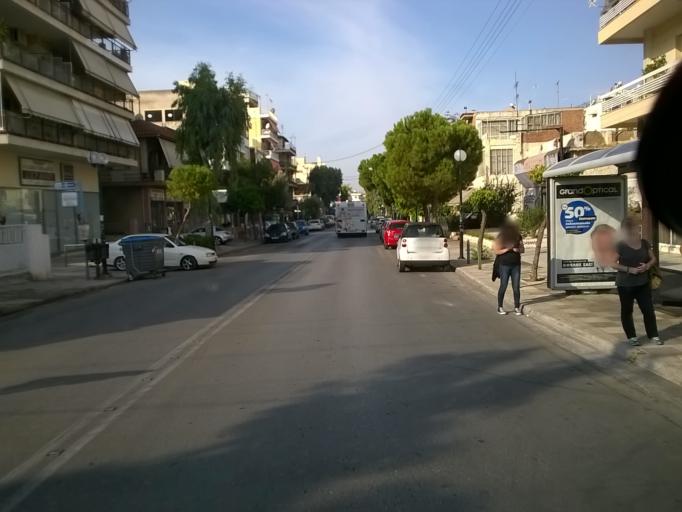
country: GR
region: Attica
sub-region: Nomarchia Athinas
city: Alimos
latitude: 37.9235
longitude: 23.7198
